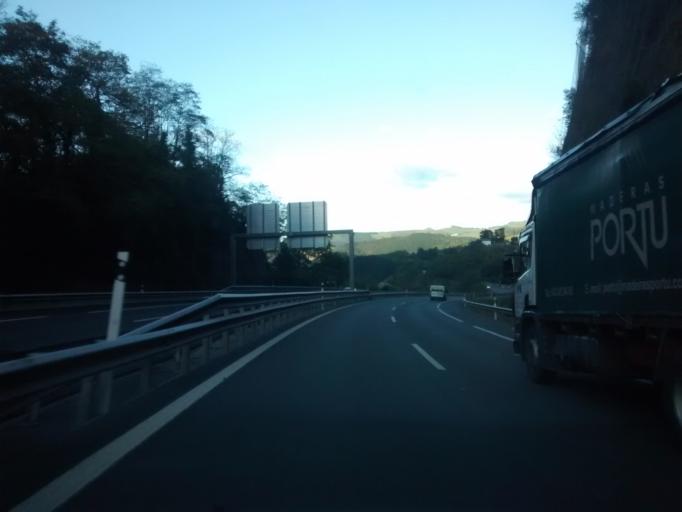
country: ES
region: Basque Country
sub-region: Provincia de Guipuzcoa
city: Elgoibar
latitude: 43.2025
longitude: -2.4278
